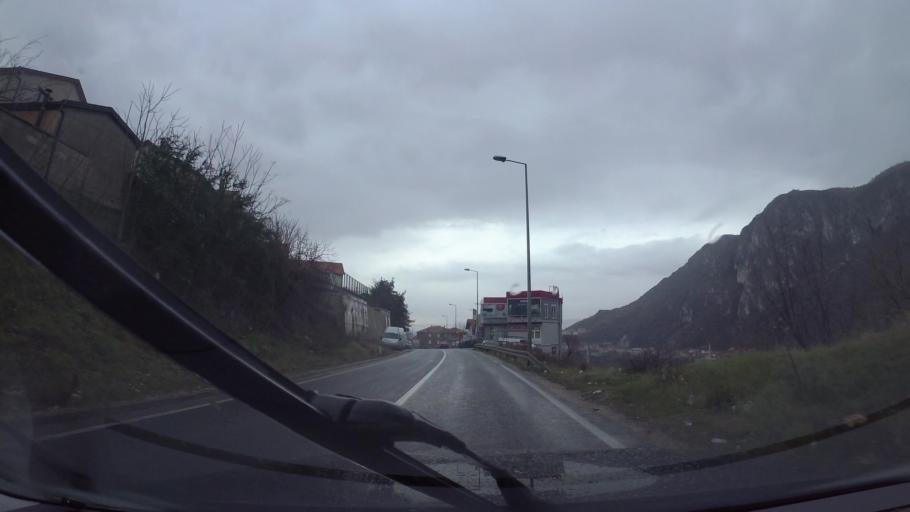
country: BA
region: Federation of Bosnia and Herzegovina
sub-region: Hercegovacko-Bosanski Kanton
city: Mostar
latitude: 43.3348
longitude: 17.8192
